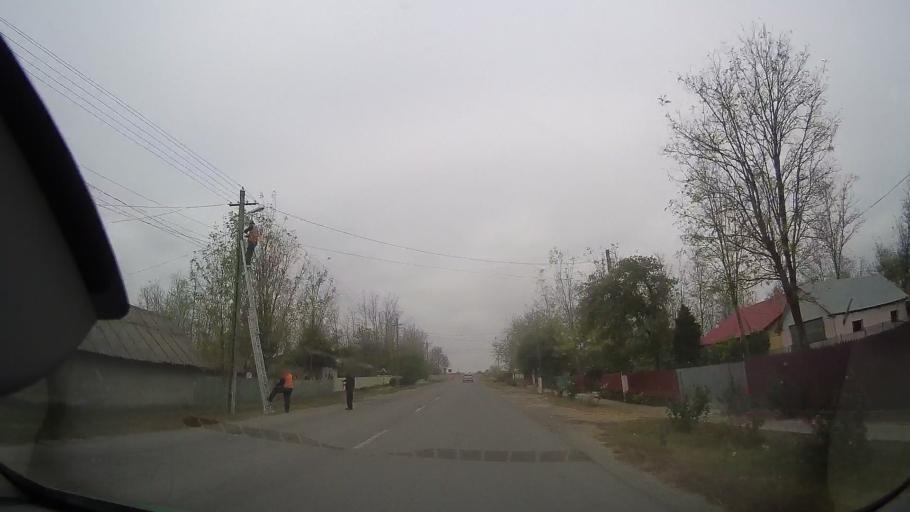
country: RO
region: Ialomita
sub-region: Comuna Grivita
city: Grivita
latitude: 44.7397
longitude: 27.2808
